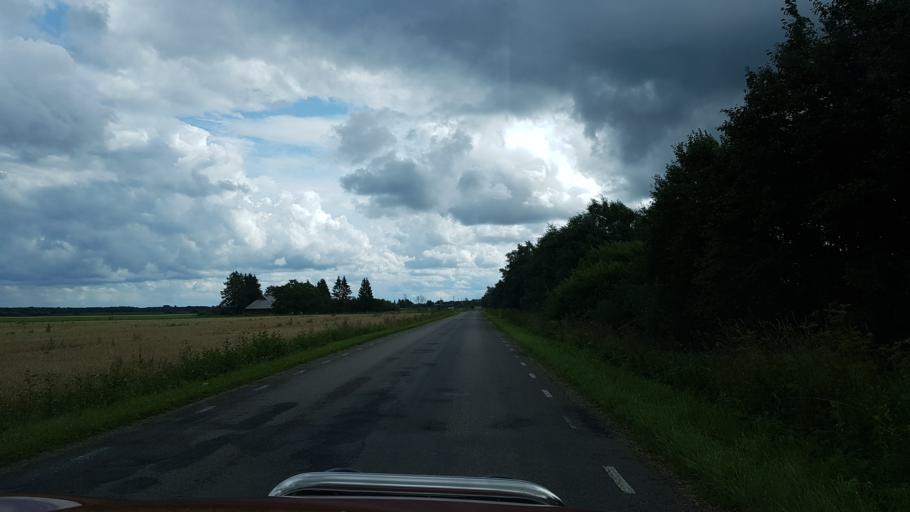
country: EE
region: Laeaene
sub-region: Lihula vald
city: Lihula
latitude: 58.7194
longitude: 23.9798
